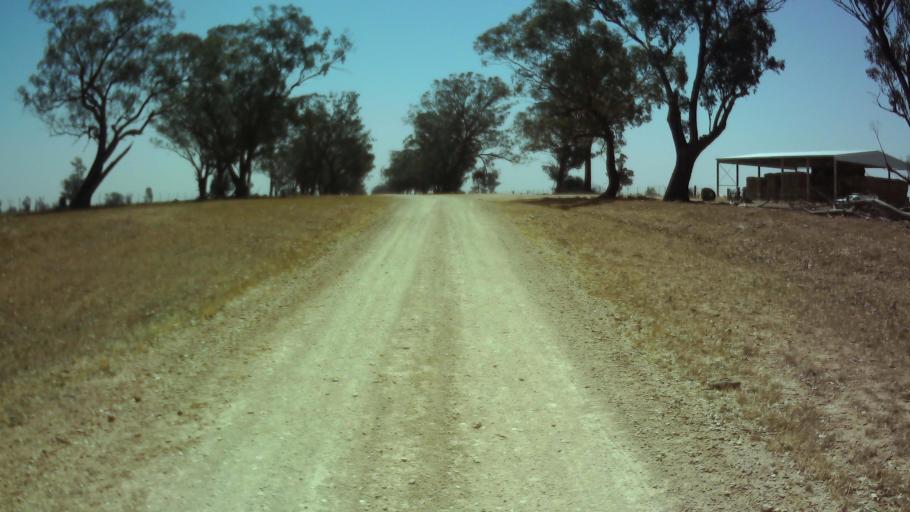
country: AU
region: New South Wales
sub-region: Weddin
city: Grenfell
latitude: -34.0134
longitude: 147.8961
